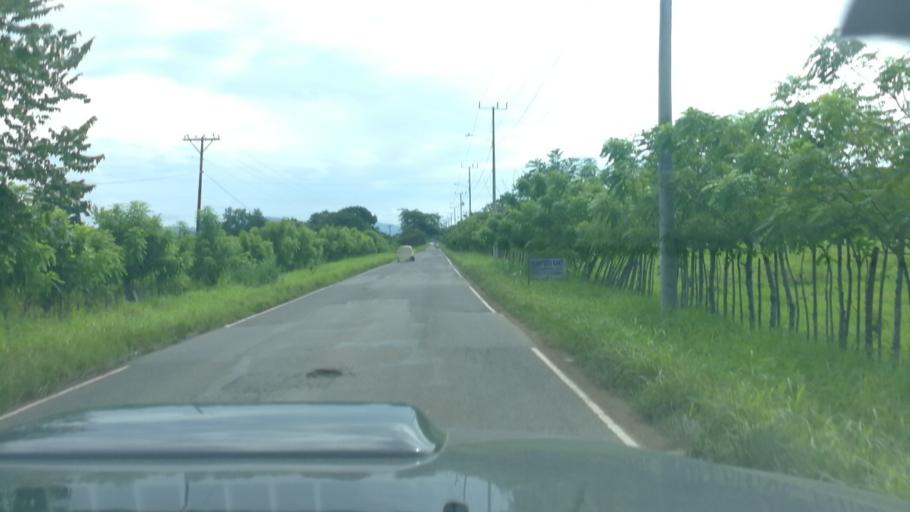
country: PA
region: Panama
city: Los Lotes
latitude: 9.1055
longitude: -79.2709
